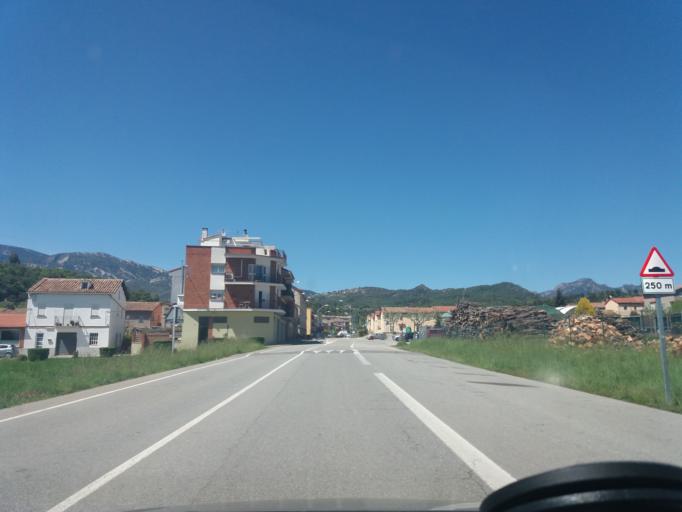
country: ES
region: Catalonia
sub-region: Provincia de Barcelona
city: Avia
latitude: 42.0680
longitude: 1.8702
